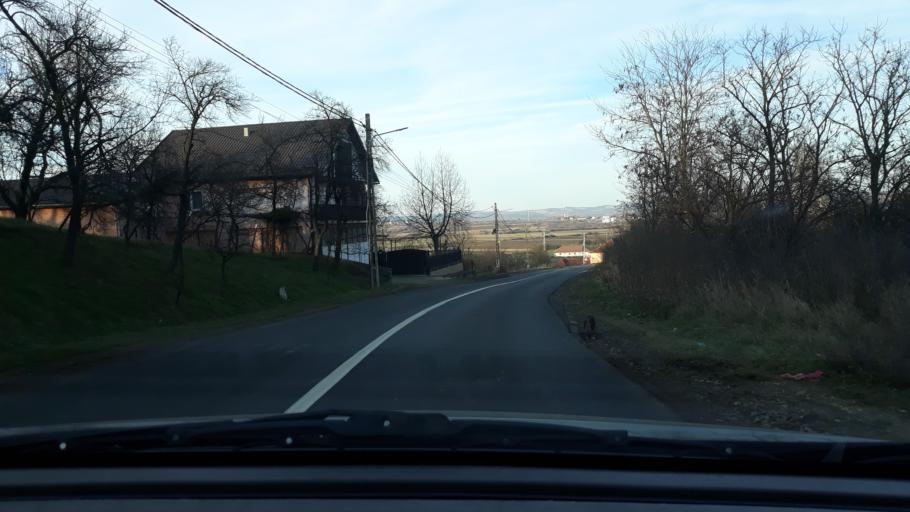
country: RO
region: Salaj
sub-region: Comuna Marca
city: Marca
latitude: 47.2275
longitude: 22.5524
